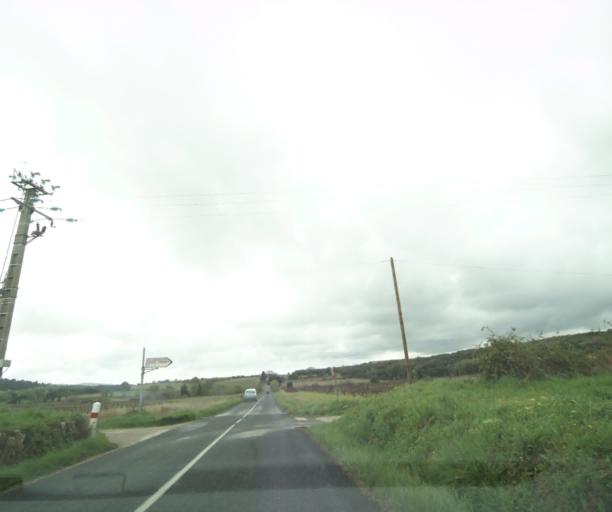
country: FR
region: Languedoc-Roussillon
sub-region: Departement de l'Herault
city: Cournonsec
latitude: 43.5363
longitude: 3.6979
